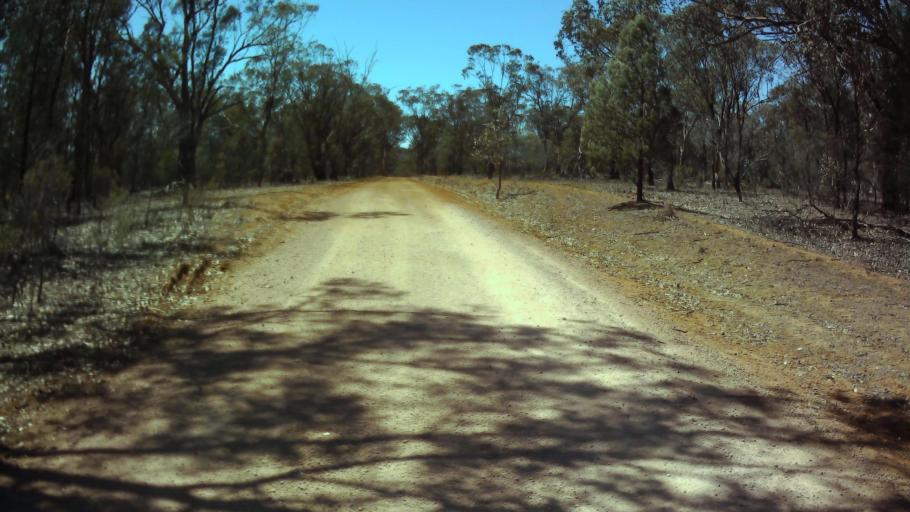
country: AU
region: New South Wales
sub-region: Weddin
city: Grenfell
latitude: -33.9456
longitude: 148.0804
